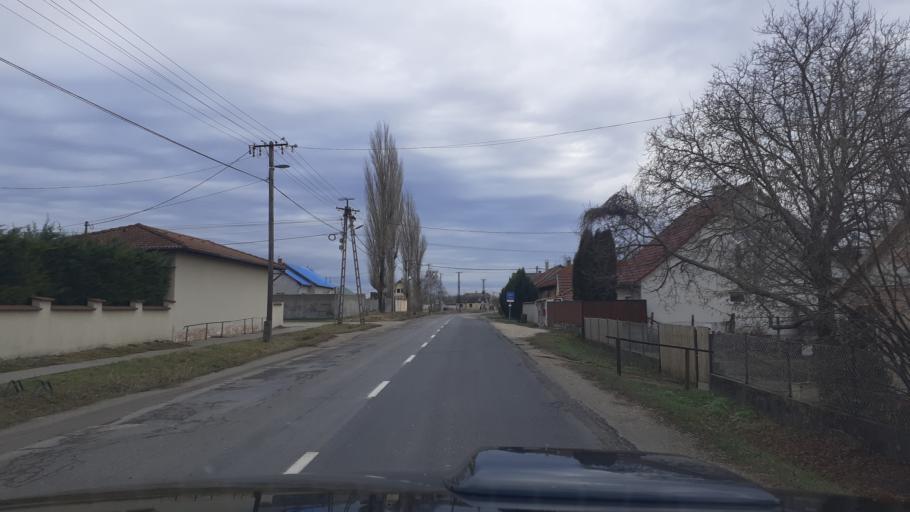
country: HU
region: Fejer
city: Sarosd
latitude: 47.0383
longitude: 18.6551
